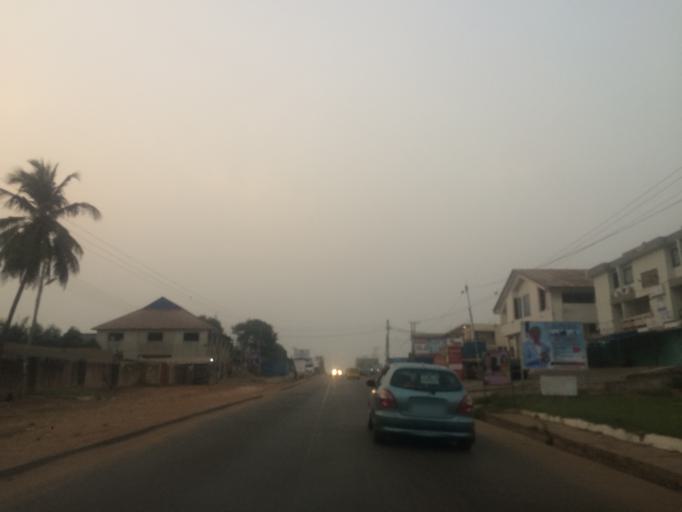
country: GH
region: Greater Accra
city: Teshi Old Town
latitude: 5.5967
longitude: -0.1018
